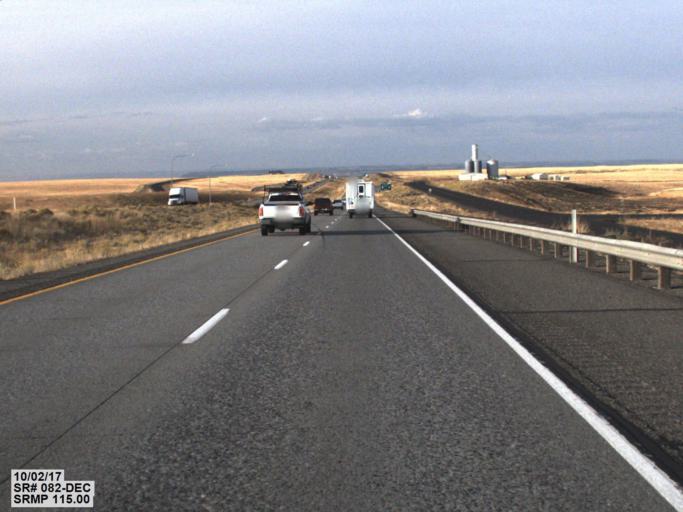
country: US
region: Washington
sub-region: Benton County
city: Highland
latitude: 46.1336
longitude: -119.2020
